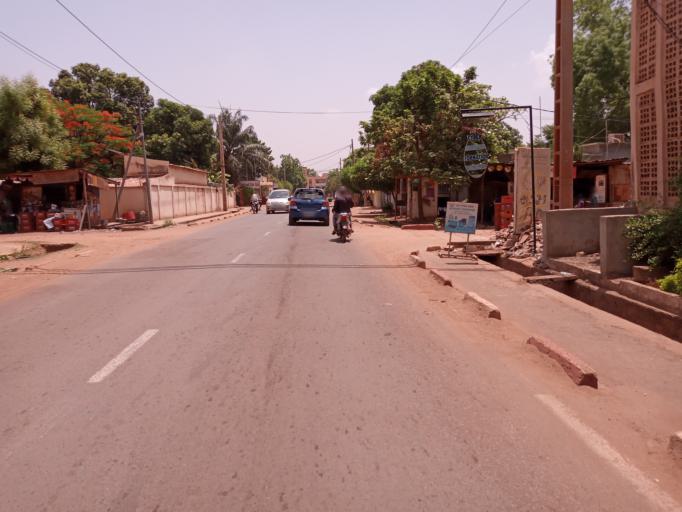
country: ML
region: Bamako
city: Bamako
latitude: 12.6459
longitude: -7.9773
